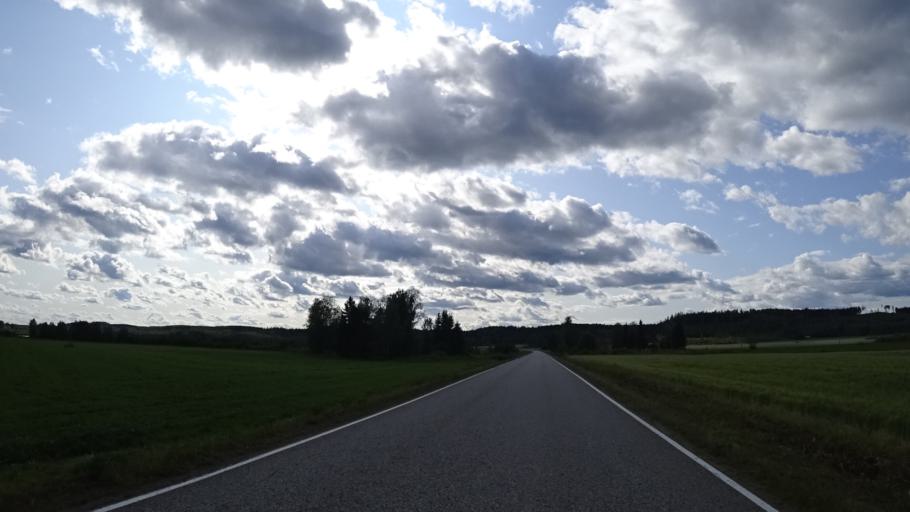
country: RU
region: Republic of Karelia
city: Vyartsilya
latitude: 62.2212
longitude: 30.6252
